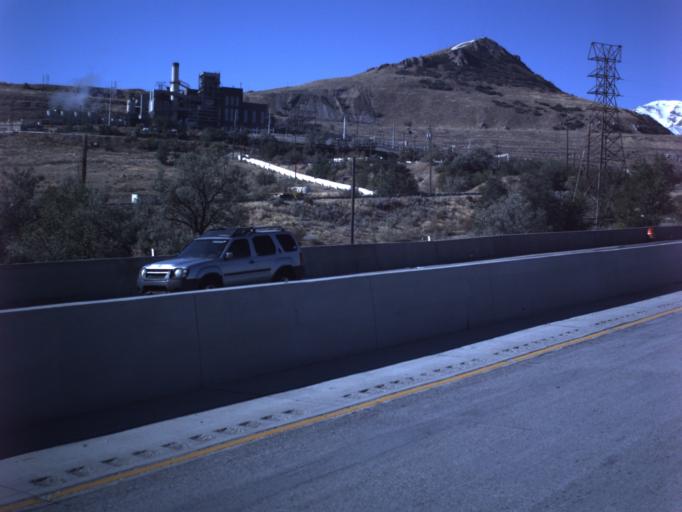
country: US
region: Utah
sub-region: Salt Lake County
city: Magna
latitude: 40.7179
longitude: -112.1171
